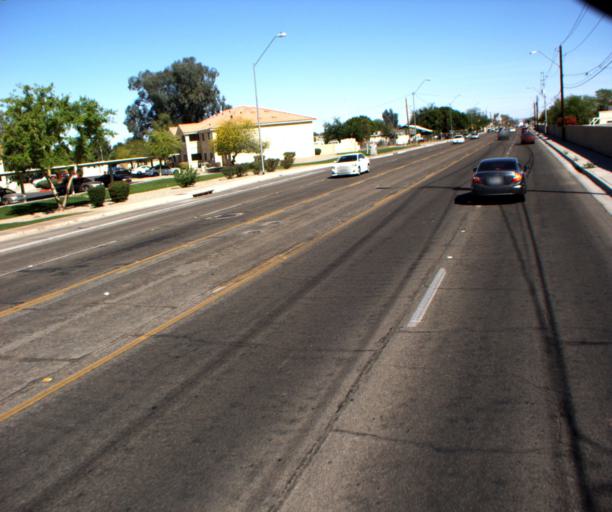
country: US
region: Arizona
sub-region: Yuma County
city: Yuma
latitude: 32.6938
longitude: -114.6504
